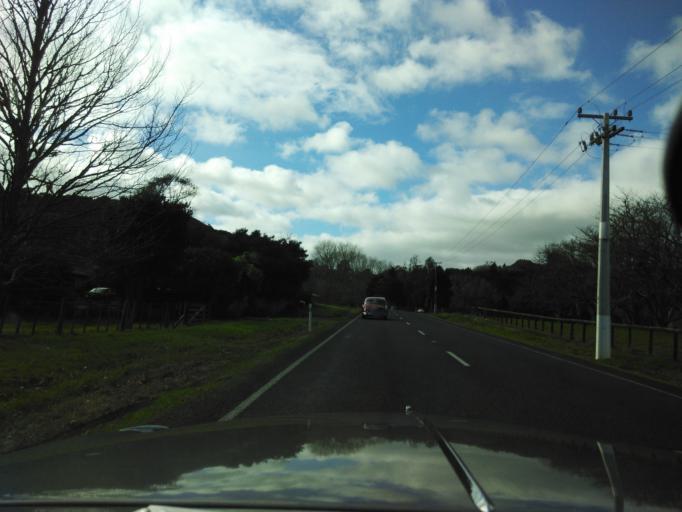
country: NZ
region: Auckland
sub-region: Auckland
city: Pukekohe East
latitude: -37.1420
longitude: 174.9811
